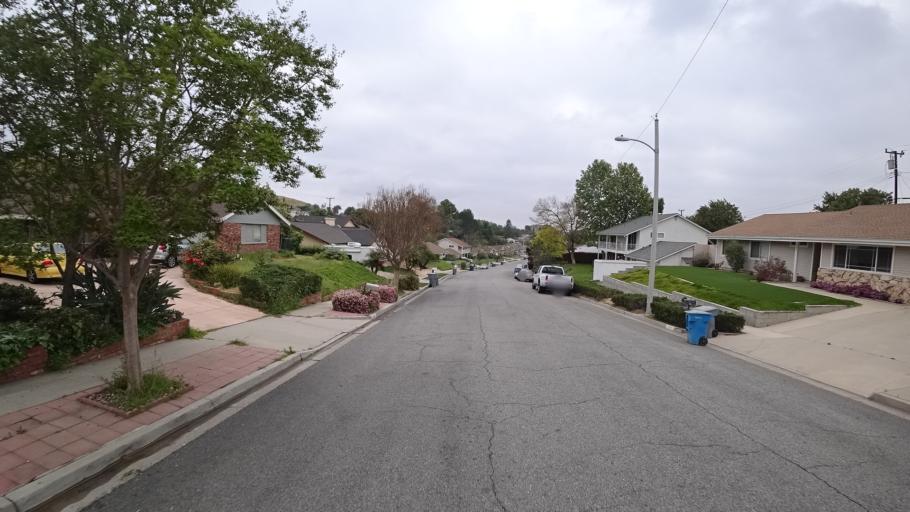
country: US
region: California
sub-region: Ventura County
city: Thousand Oaks
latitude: 34.2049
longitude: -118.8696
